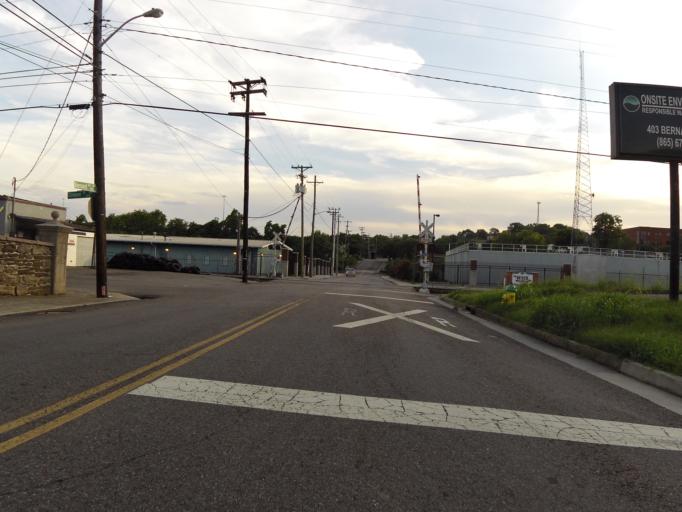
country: US
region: Tennessee
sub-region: Knox County
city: Knoxville
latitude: 35.9755
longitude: -83.9291
